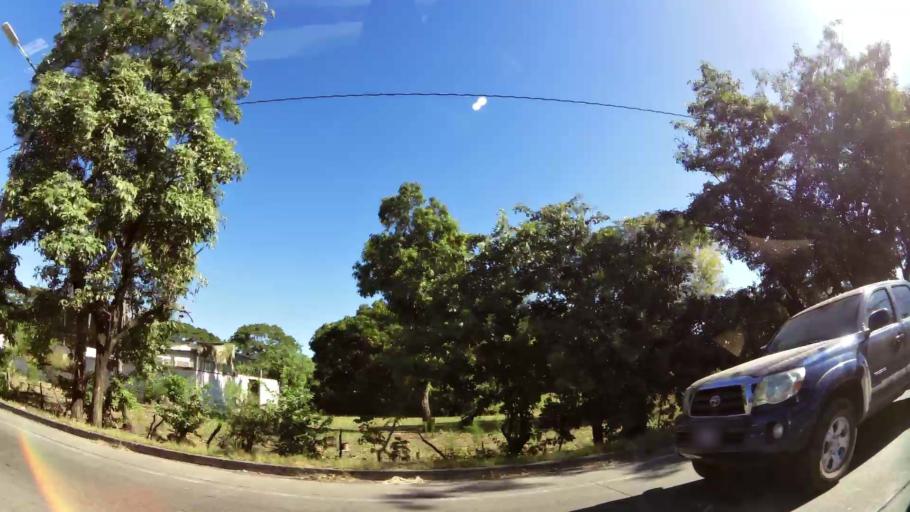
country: SV
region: San Miguel
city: San Miguel
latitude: 13.4594
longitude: -88.1475
